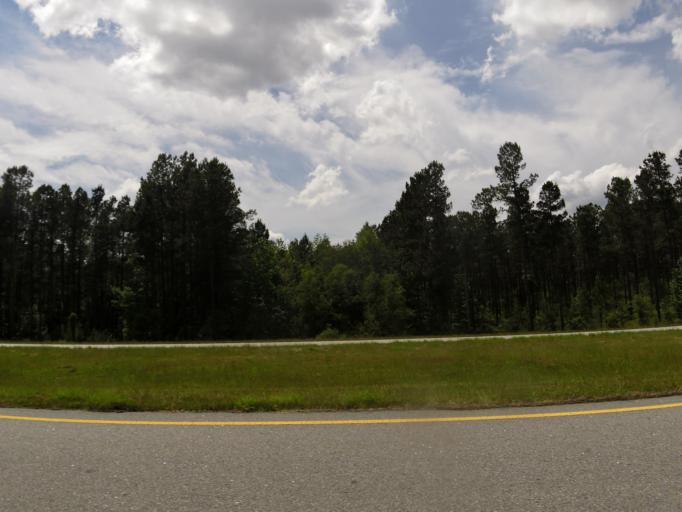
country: US
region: Georgia
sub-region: Emanuel County
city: Swainsboro
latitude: 32.7037
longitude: -82.3909
